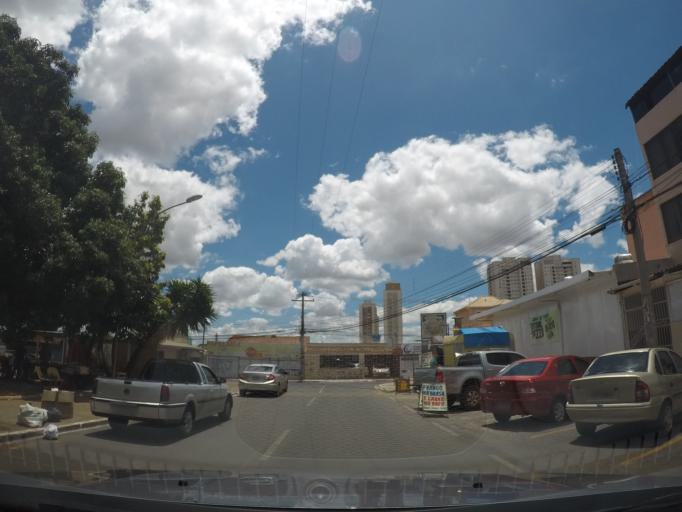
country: BR
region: Federal District
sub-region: Brasilia
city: Brasilia
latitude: -15.8412
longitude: -47.9806
